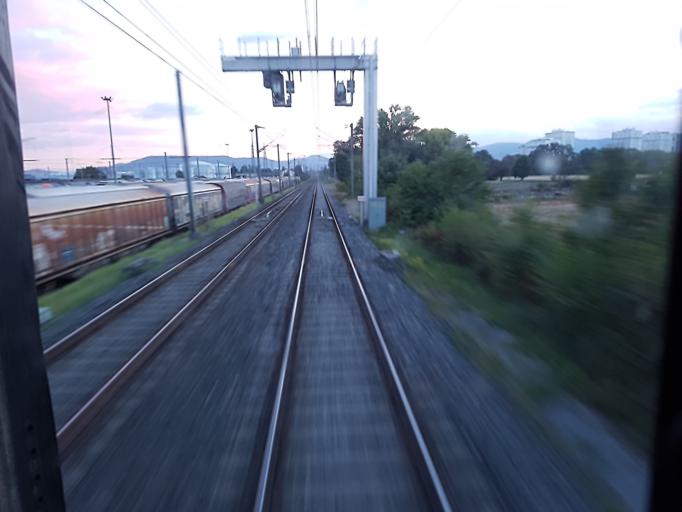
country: FR
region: Auvergne
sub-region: Departement du Puy-de-Dome
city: Gerzat
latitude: 45.8177
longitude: 3.1355
